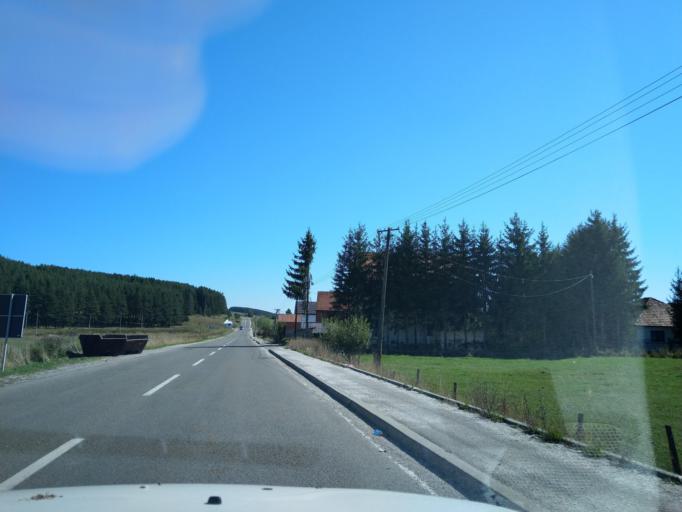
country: RS
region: Central Serbia
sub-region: Zlatiborski Okrug
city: Sjenica
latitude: 43.2705
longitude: 20.0213
